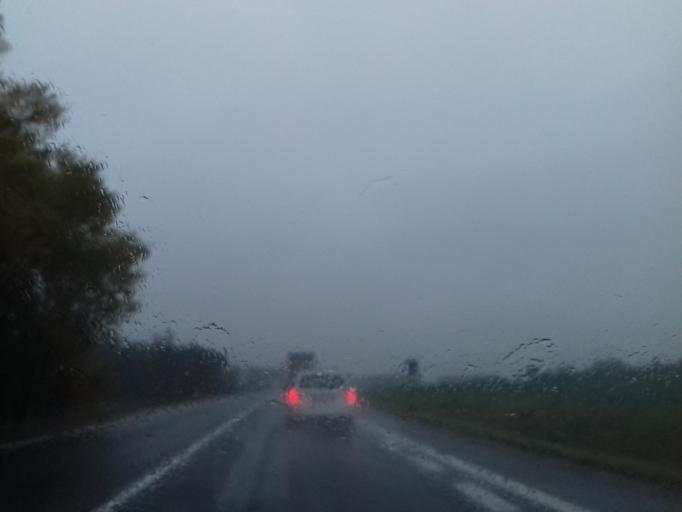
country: CZ
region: Pardubicky
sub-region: Okres Svitavy
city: Svitavy
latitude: 49.8160
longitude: 16.4136
